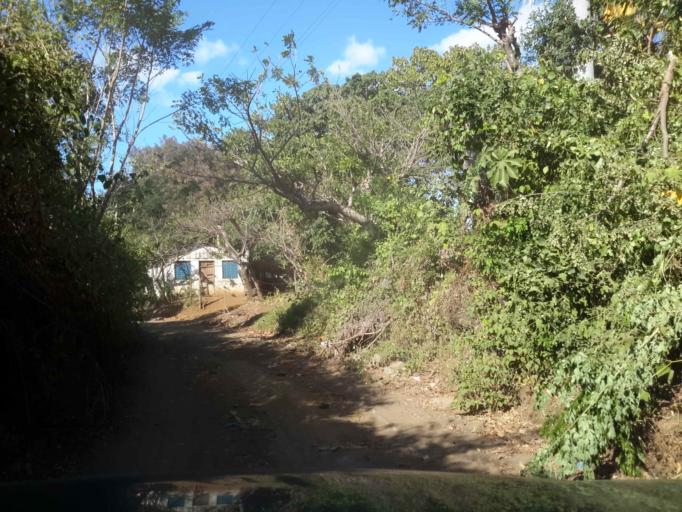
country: NI
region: Managua
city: Managua
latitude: 12.0691
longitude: -86.2529
